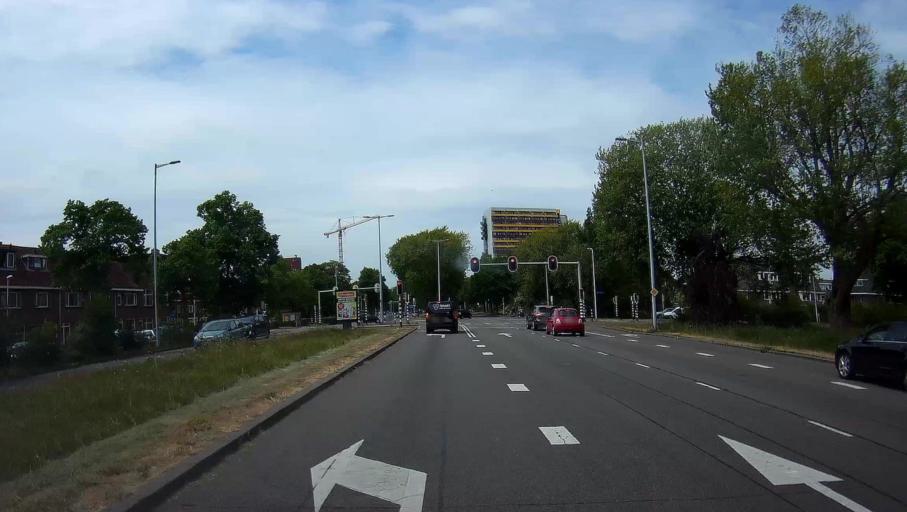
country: NL
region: Utrecht
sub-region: Gemeente Utrecht
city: Utrecht
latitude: 52.1055
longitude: 5.1216
